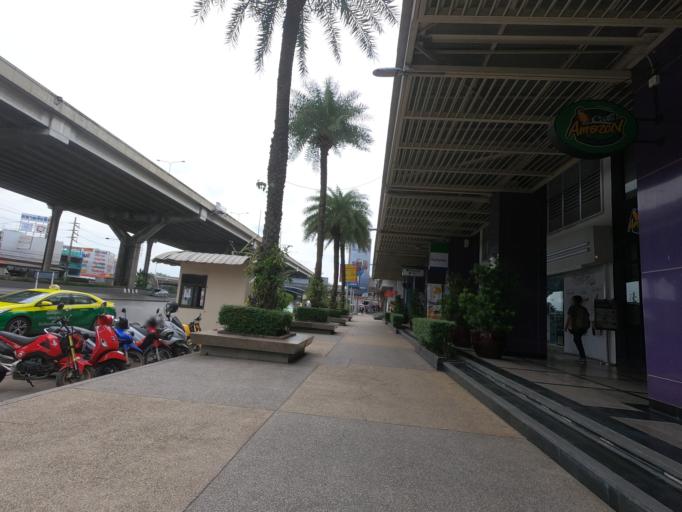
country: TH
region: Phra Nakhon Si Ayutthaya
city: Ban Bang Kadi Pathum Thani
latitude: 13.9882
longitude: 100.6086
